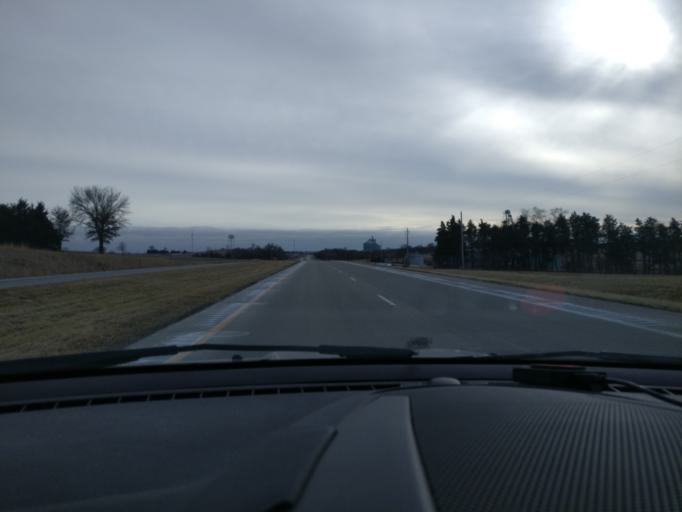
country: US
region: Nebraska
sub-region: Saunders County
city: Wahoo
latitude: 41.0714
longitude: -96.6403
